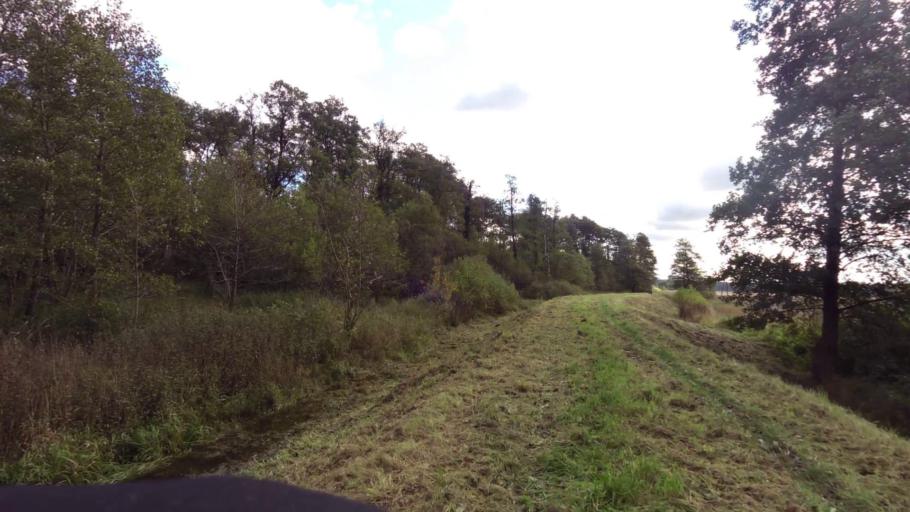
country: PL
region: West Pomeranian Voivodeship
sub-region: Powiat bialogardzki
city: Bialogard
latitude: 53.9996
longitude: 16.0190
